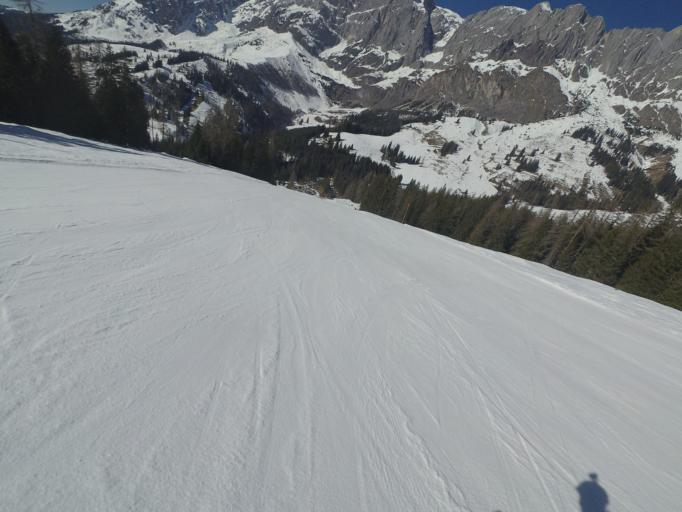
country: AT
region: Salzburg
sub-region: Politischer Bezirk Sankt Johann im Pongau
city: Muhlbach am Hochkonig
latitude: 47.3973
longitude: 13.1211
